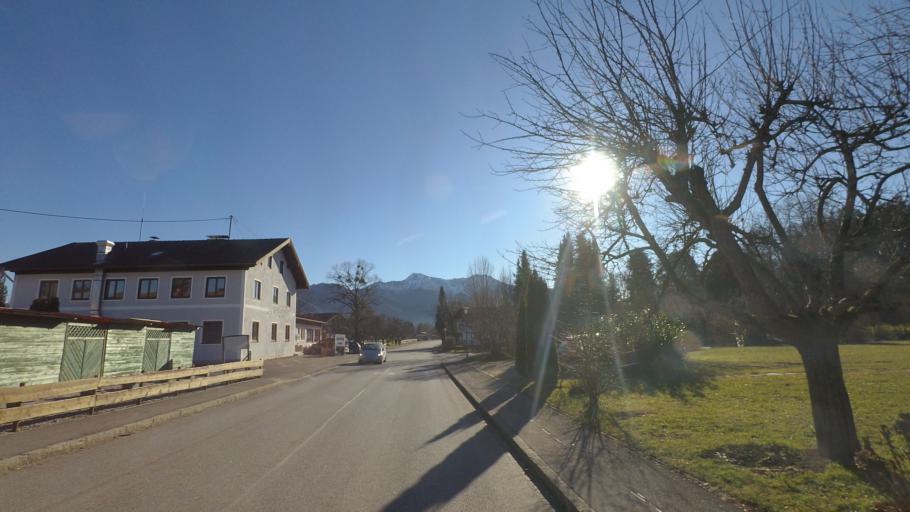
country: DE
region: Bavaria
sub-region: Upper Bavaria
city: Ubersee
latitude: 47.8177
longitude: 12.4822
